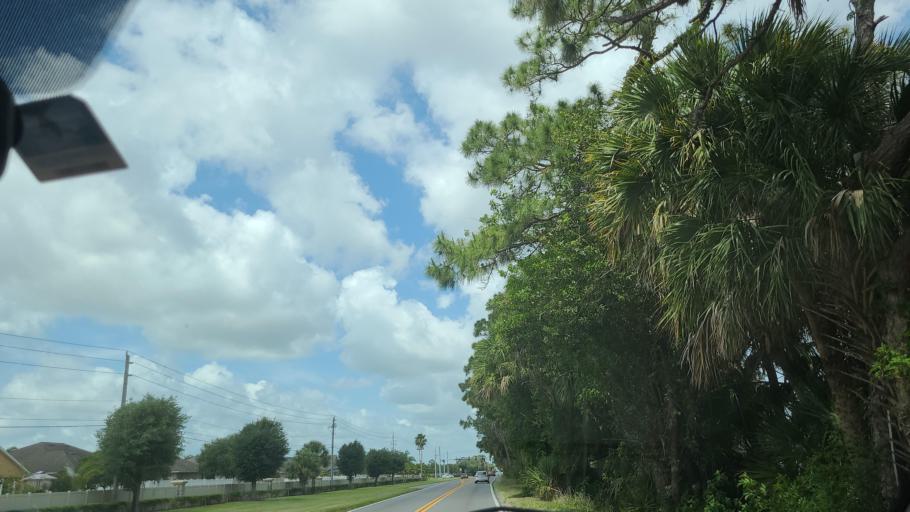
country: US
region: Florida
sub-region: Brevard County
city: June Park
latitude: 27.9990
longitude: -80.7137
